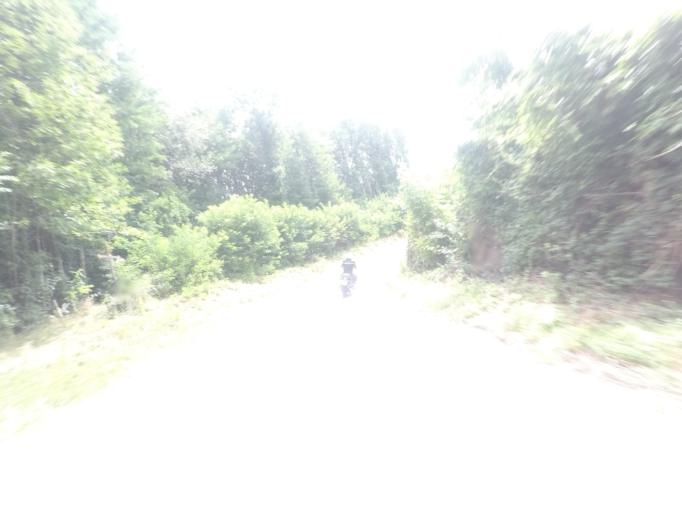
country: IT
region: Tuscany
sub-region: Provincia di Lucca
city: Castelnuovo di Garfagnana
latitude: 44.1121
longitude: 10.3896
